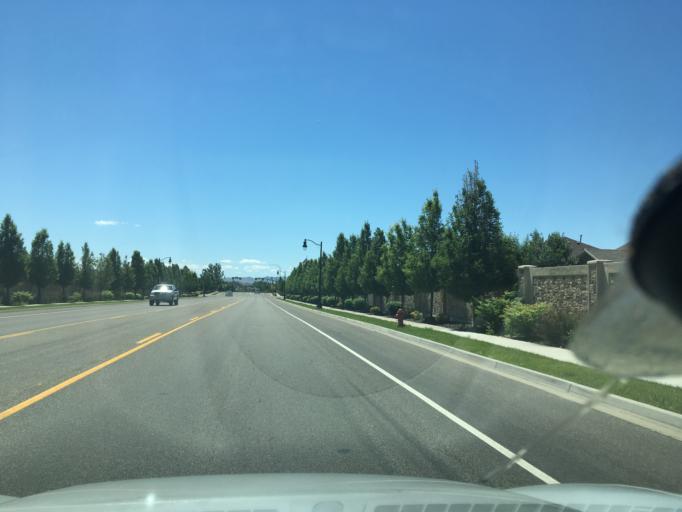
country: US
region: Utah
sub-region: Davis County
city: Layton
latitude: 41.0519
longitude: -111.9748
